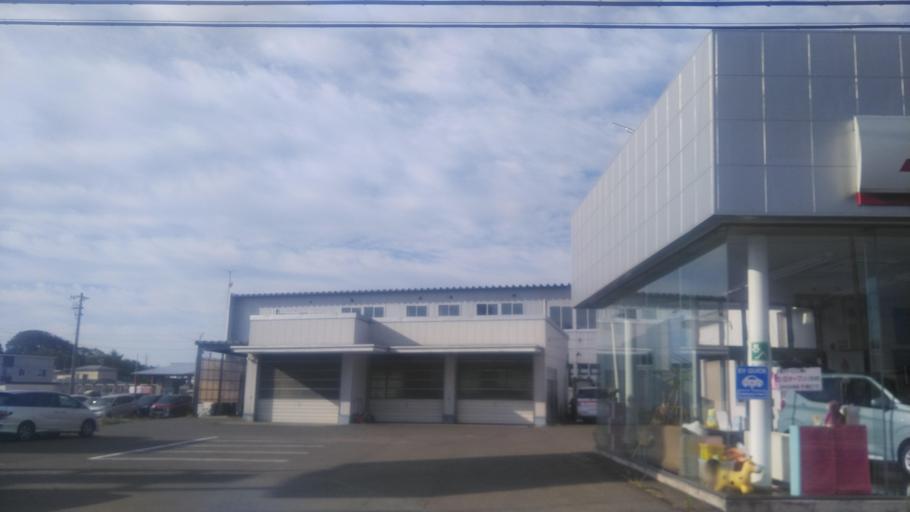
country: JP
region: Akita
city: Noshiromachi
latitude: 40.1869
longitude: 140.0440
